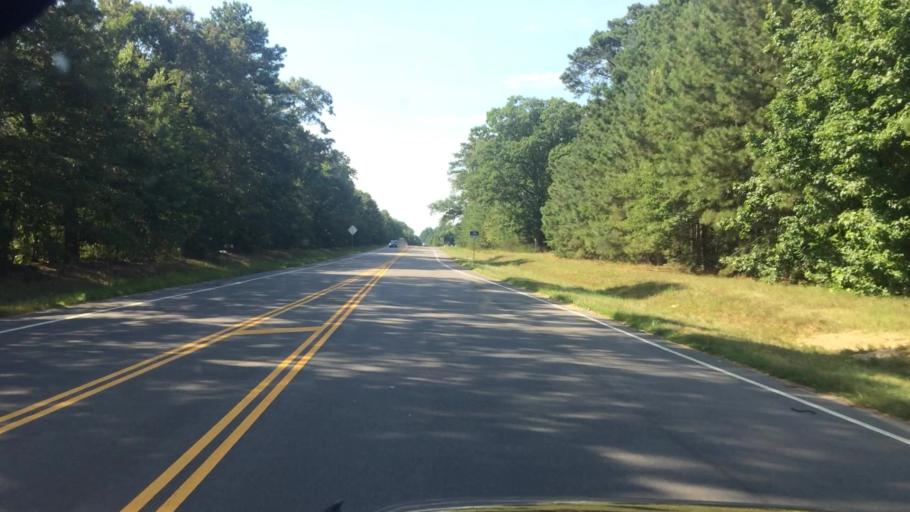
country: US
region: Virginia
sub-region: City of Williamsburg
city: Williamsburg
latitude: 37.2898
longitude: -76.7214
